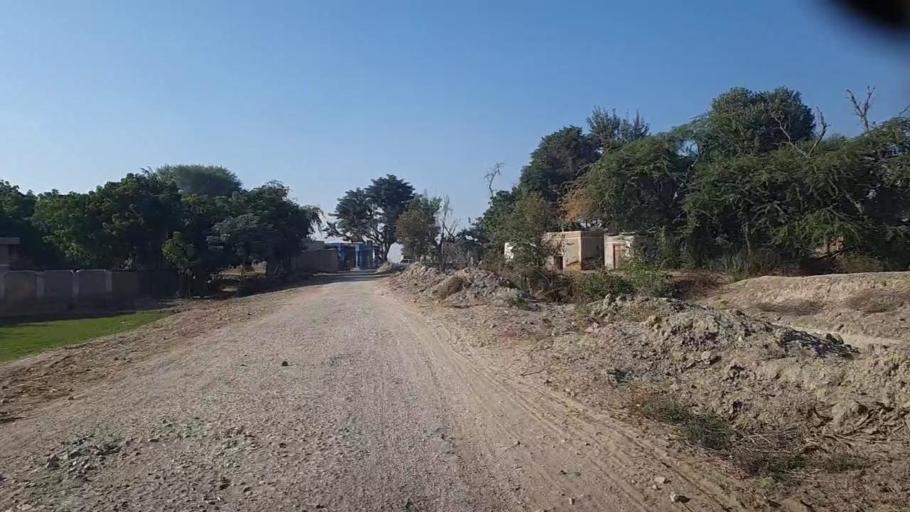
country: PK
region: Sindh
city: Darya Khan Marri
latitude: 26.6951
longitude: 68.3465
